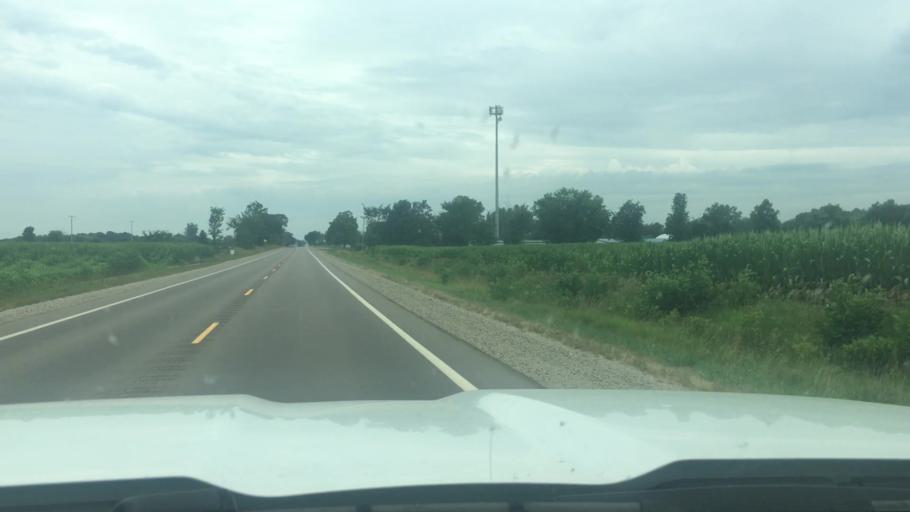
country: US
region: Michigan
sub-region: Clinton County
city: Saint Johns
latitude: 43.0016
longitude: -84.6483
